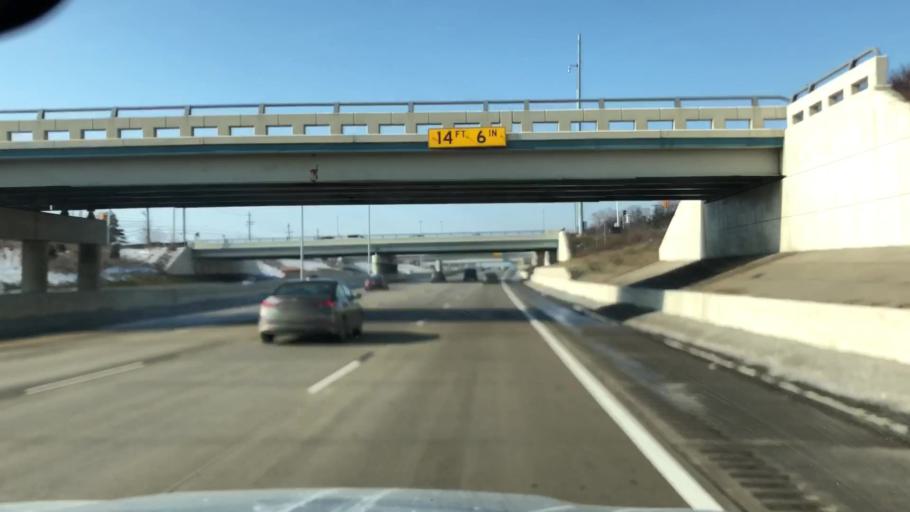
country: US
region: Michigan
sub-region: Wayne County
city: Livonia
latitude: 42.3828
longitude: -83.3716
